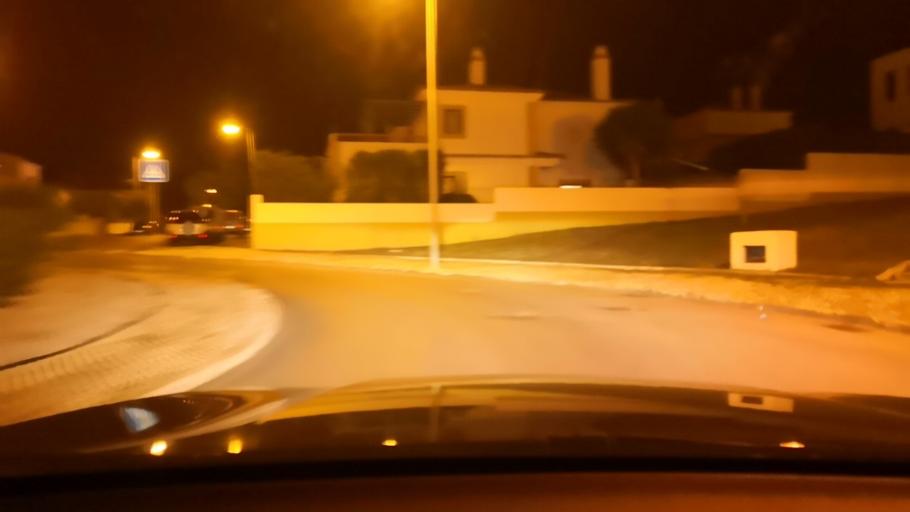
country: PT
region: Setubal
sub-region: Setubal
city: Setubal
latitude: 38.5433
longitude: -8.8555
